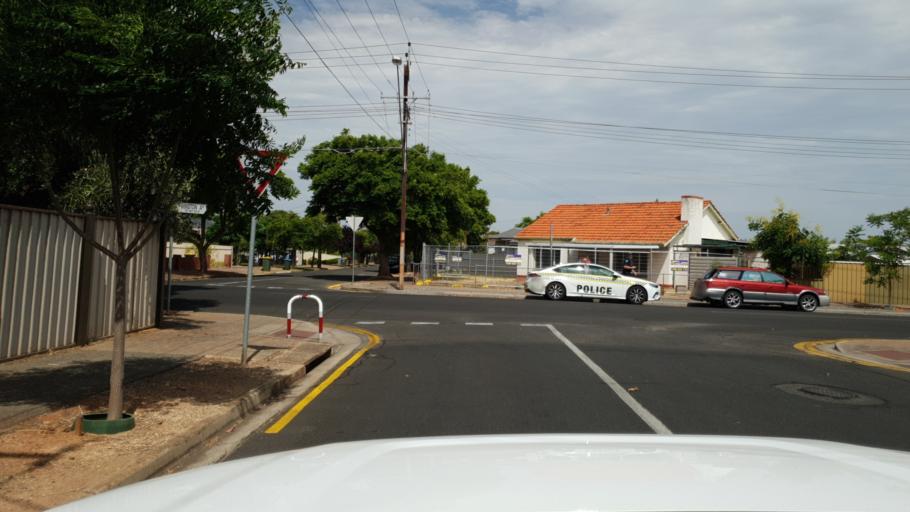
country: AU
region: South Australia
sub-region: Mitcham
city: Clarence Gardens
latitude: -34.9737
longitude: 138.5824
